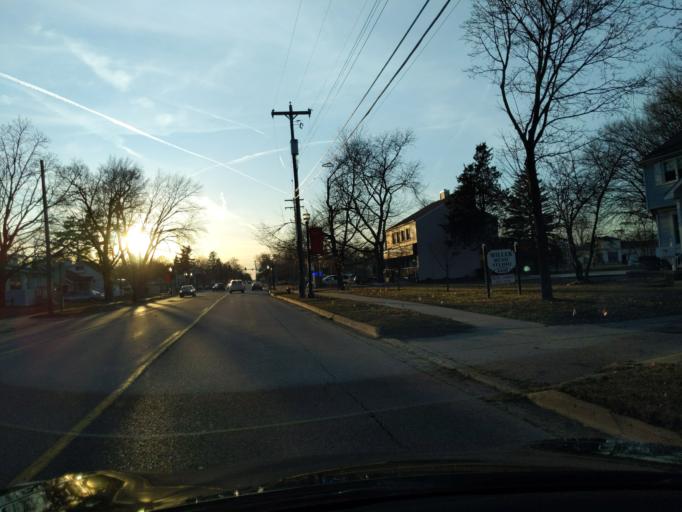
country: US
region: Michigan
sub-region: Ingham County
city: Holt
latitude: 42.6403
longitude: -84.5212
